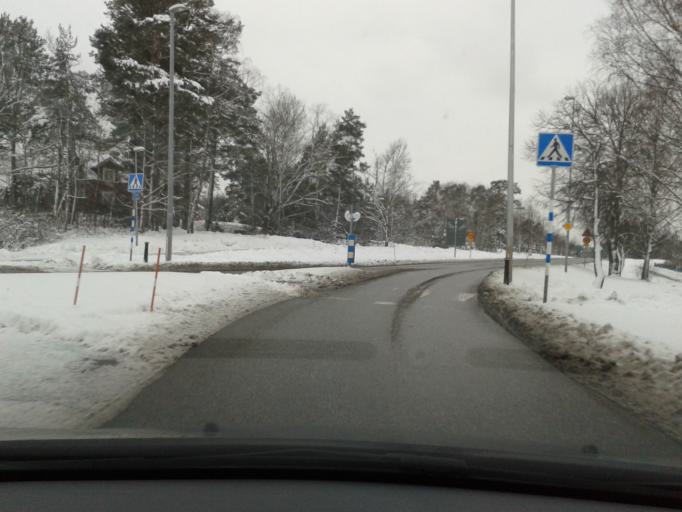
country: SE
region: Stockholm
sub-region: Nacka Kommun
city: Saltsjobaden
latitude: 59.2398
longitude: 18.2953
